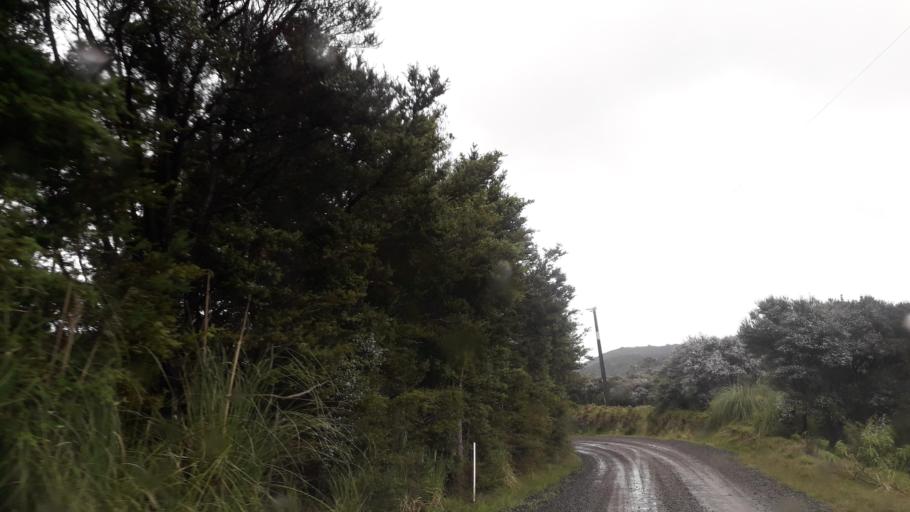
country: NZ
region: Northland
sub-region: Far North District
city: Kaitaia
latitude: -35.3801
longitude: 173.4100
